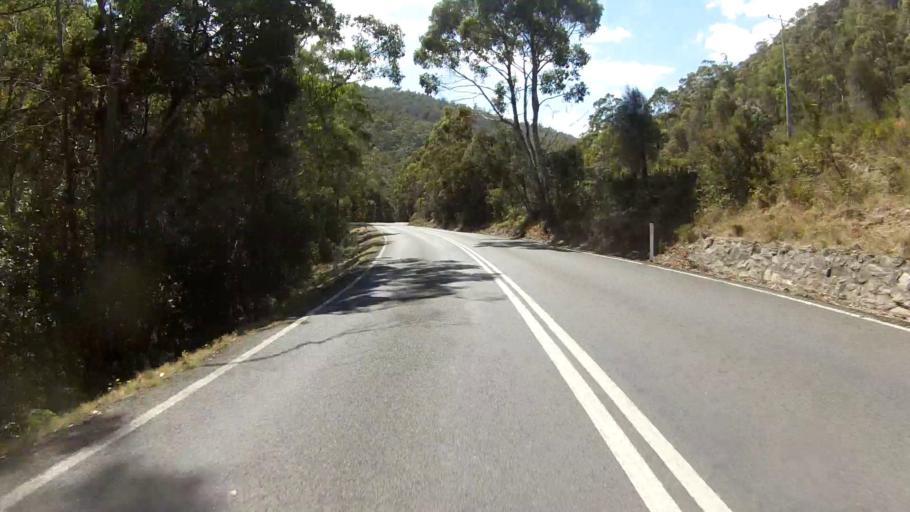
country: AU
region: Tasmania
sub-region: Derwent Valley
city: New Norfolk
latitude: -42.6789
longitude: 146.7544
